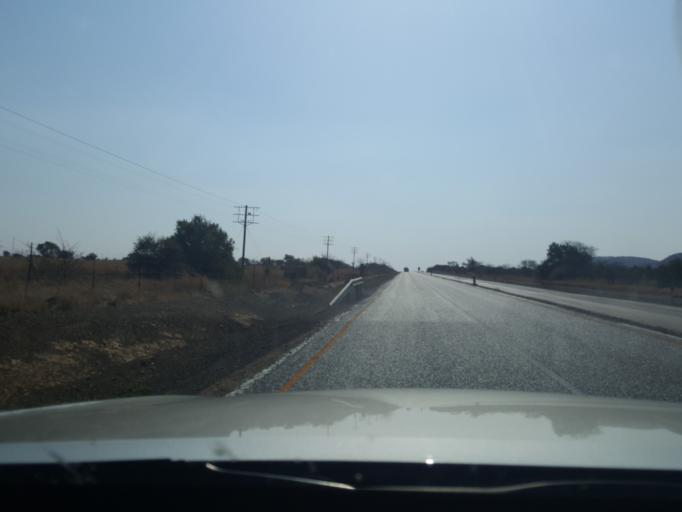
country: ZA
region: North-West
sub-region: Ngaka Modiri Molema District Municipality
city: Zeerust
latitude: -25.6177
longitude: 26.4673
